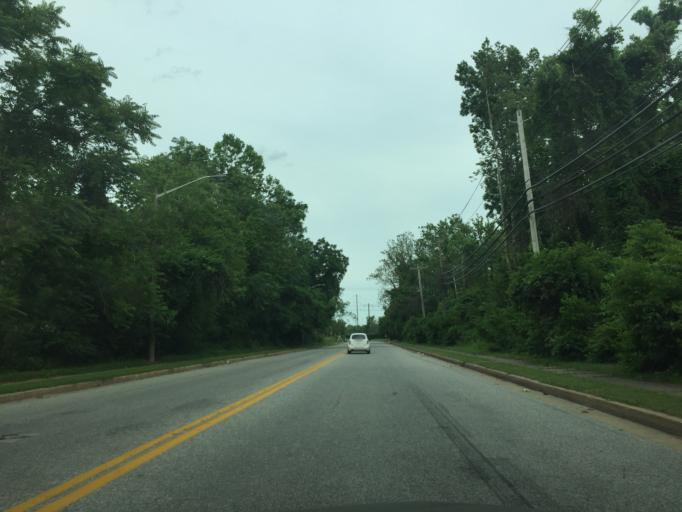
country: US
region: Maryland
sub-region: Baltimore County
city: Rossville
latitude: 39.3301
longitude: -76.4688
